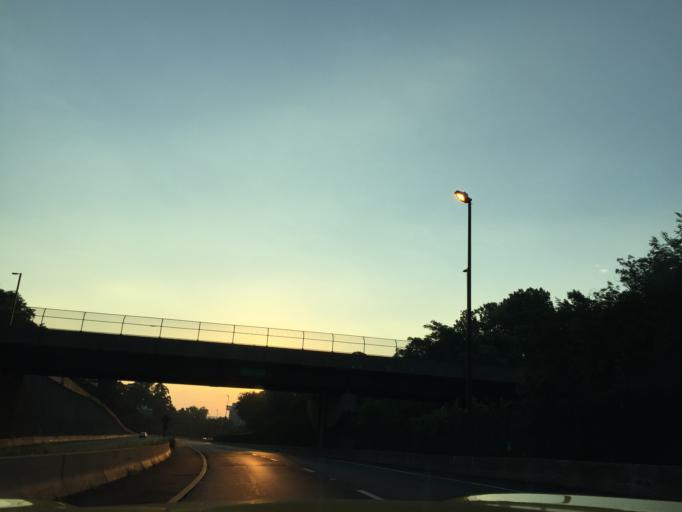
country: US
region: Virginia
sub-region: Arlington County
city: Arlington
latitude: 38.8968
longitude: -77.0813
